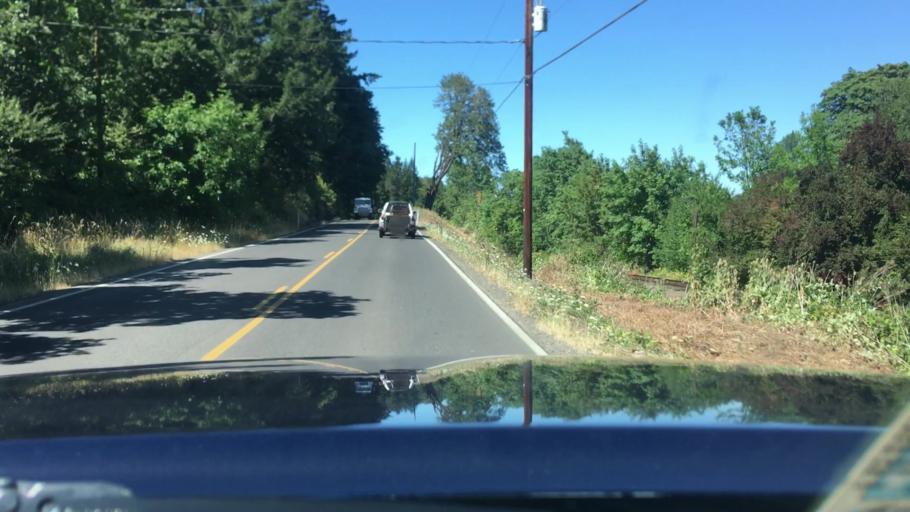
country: US
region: Oregon
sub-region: Lane County
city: Cottage Grove
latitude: 43.8173
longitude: -123.0459
